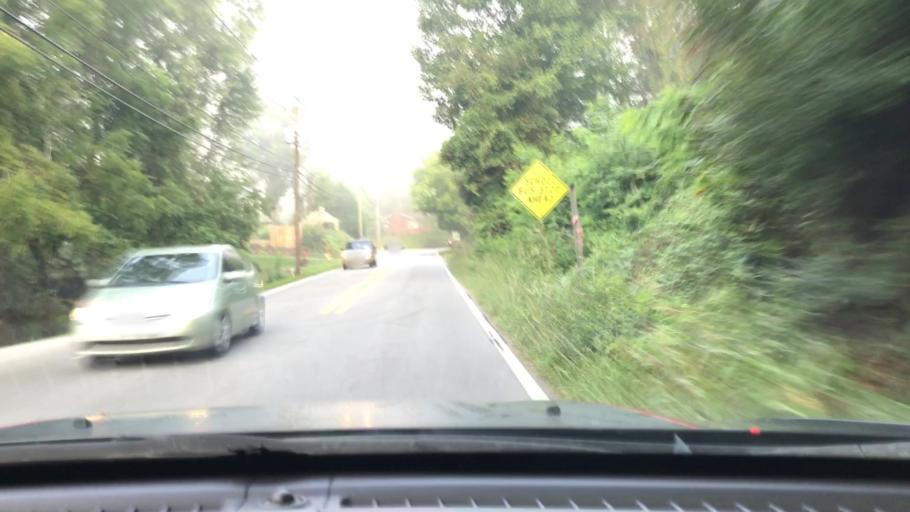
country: US
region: North Carolina
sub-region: Buncombe County
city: Woodfin
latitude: 35.6250
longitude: -82.6063
